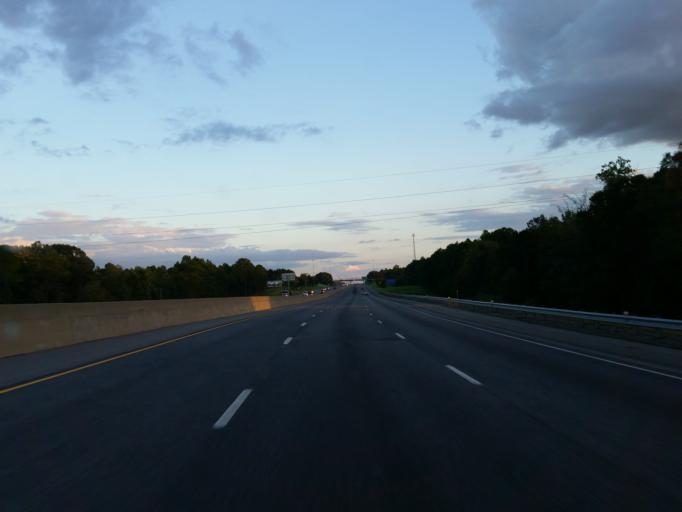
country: US
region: Georgia
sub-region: Tift County
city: Tifton
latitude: 31.5584
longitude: -83.5389
